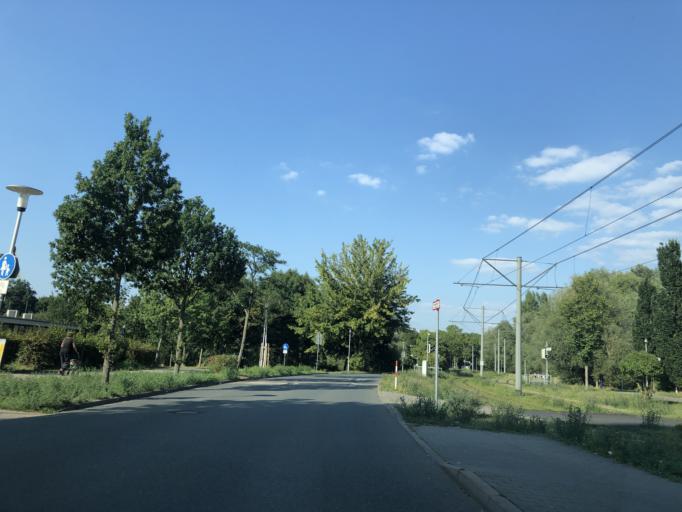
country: DE
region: Hesse
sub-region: Regierungsbezirk Darmstadt
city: Darmstadt
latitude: 49.8987
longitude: 8.6810
